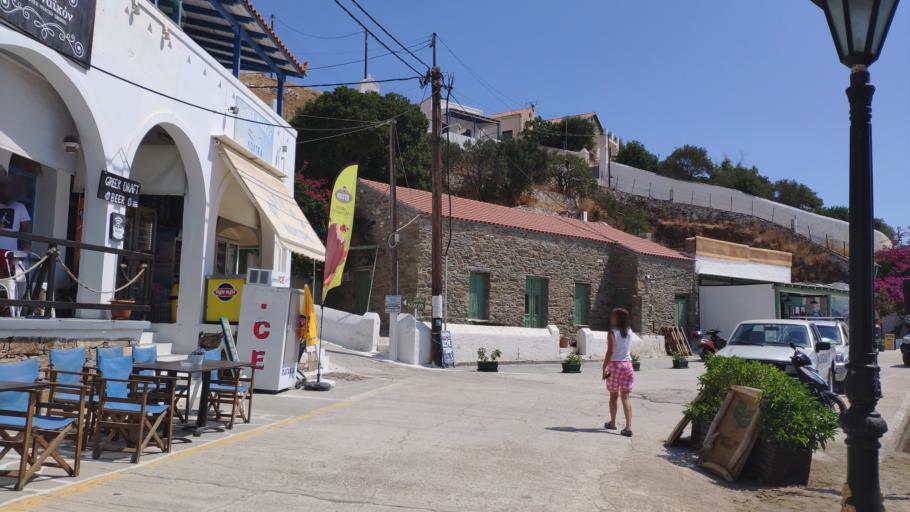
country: GR
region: South Aegean
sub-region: Nomos Kykladon
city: Kythnos
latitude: 37.4430
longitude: 24.4253
